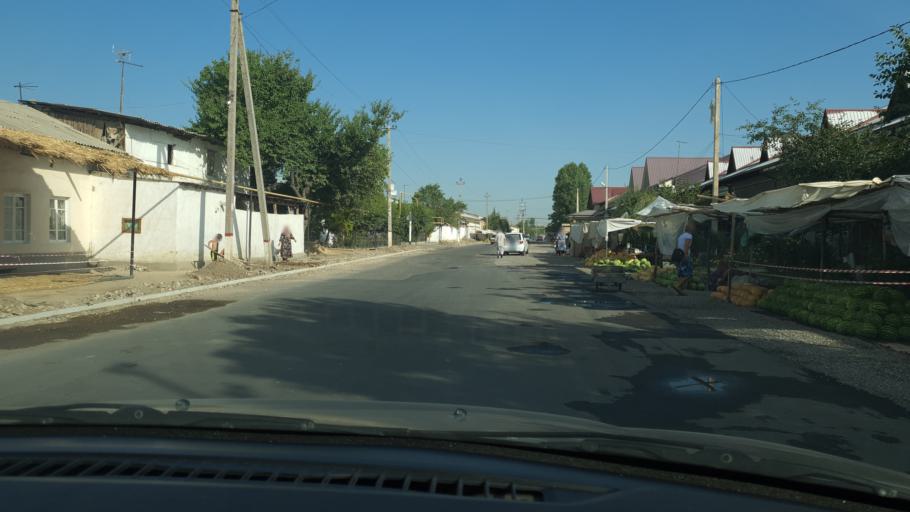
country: UZ
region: Toshkent
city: Urtaowul
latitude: 41.2019
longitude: 69.1545
